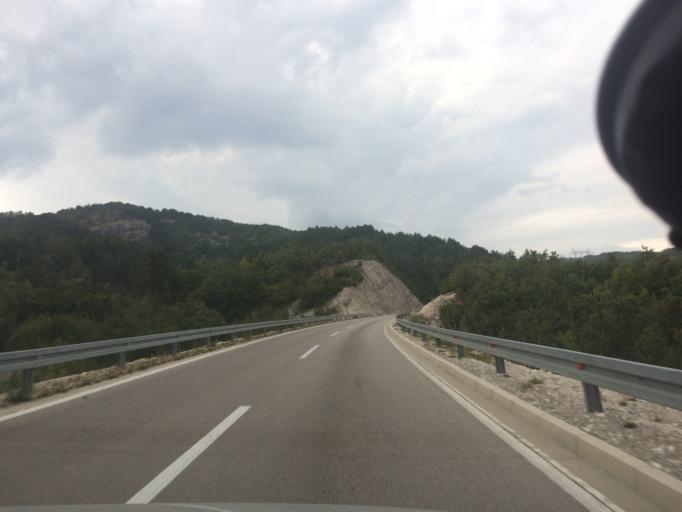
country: ME
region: Kotor
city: Risan
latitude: 42.6711
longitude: 18.6483
